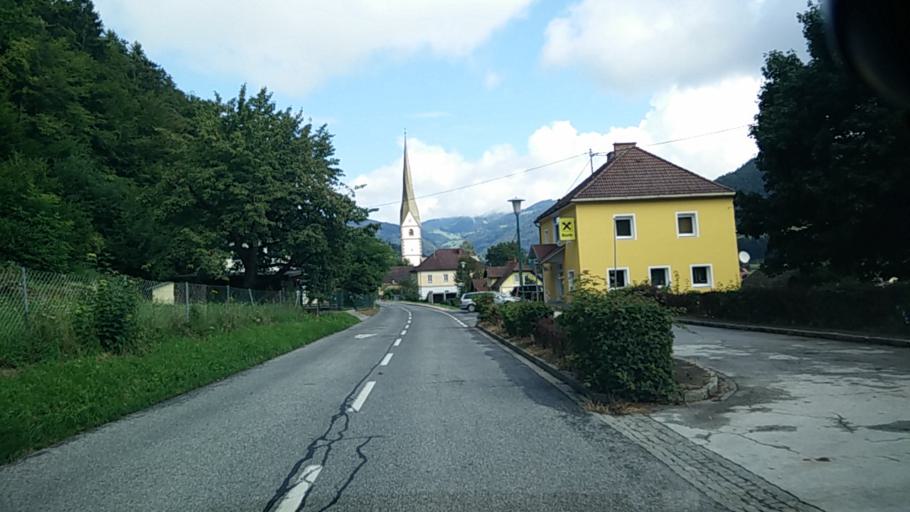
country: AT
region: Carinthia
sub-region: Politischer Bezirk Volkermarkt
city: Voelkermarkt
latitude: 46.6735
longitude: 14.5725
